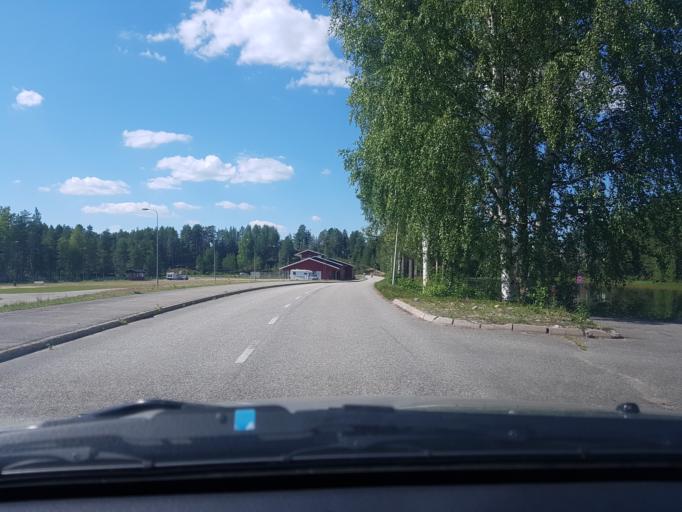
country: FI
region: Kainuu
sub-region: Kehys-Kainuu
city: Kuhmo
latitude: 64.1189
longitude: 29.5854
